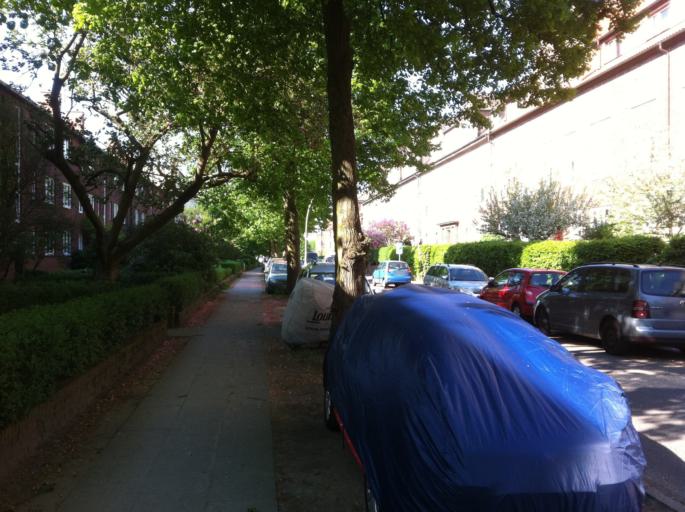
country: DE
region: Hamburg
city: Altona
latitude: 53.5516
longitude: 9.9093
